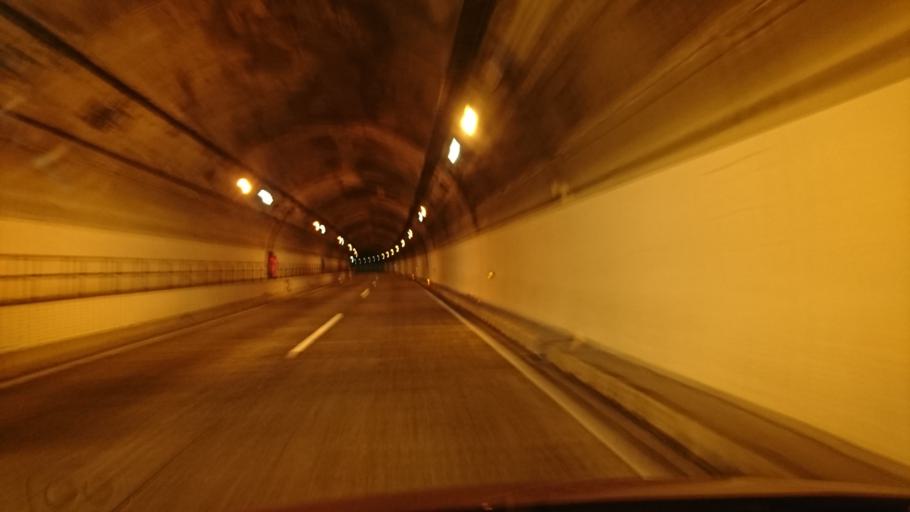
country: JP
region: Hyogo
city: Kariya
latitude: 34.7879
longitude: 134.1485
